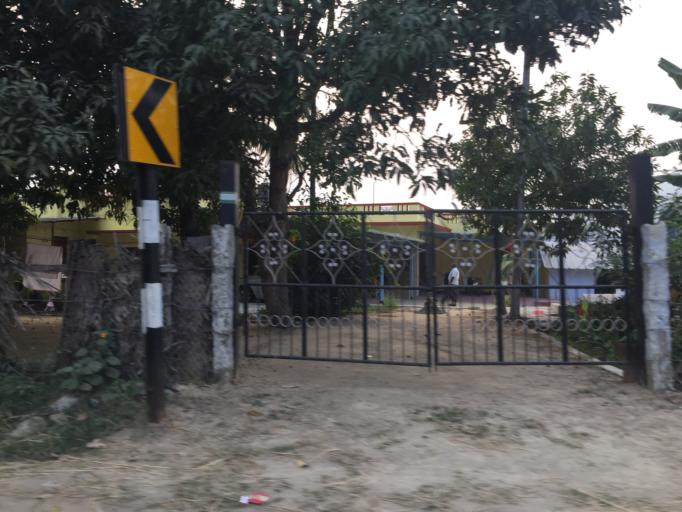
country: IN
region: Tamil Nadu
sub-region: Coimbatore
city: Perur
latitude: 10.9626
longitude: 76.7423
